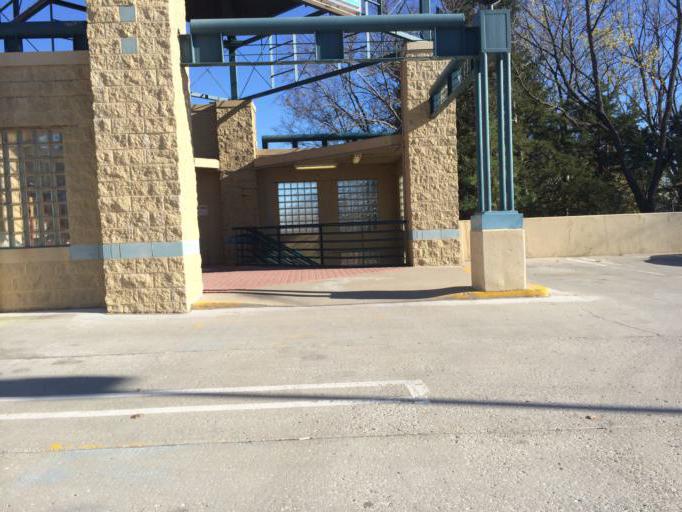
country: US
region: Kansas
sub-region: Douglas County
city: Lawrence
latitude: 38.9729
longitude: -95.2329
